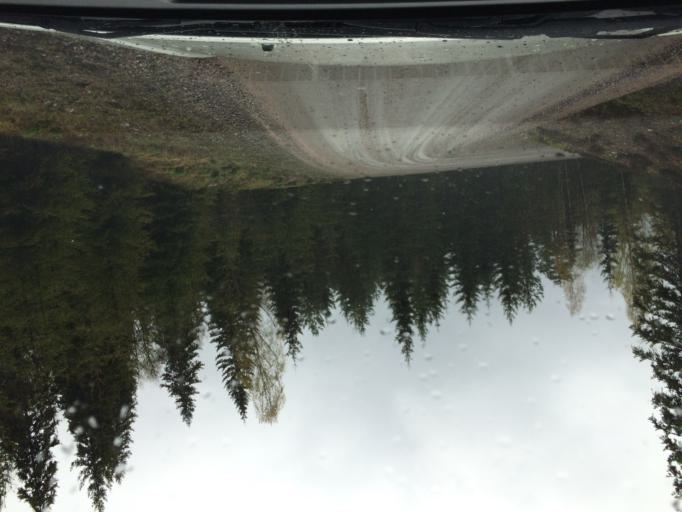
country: SE
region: OErebro
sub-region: Hallefors Kommun
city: Haellefors
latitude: 60.0166
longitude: 14.5871
